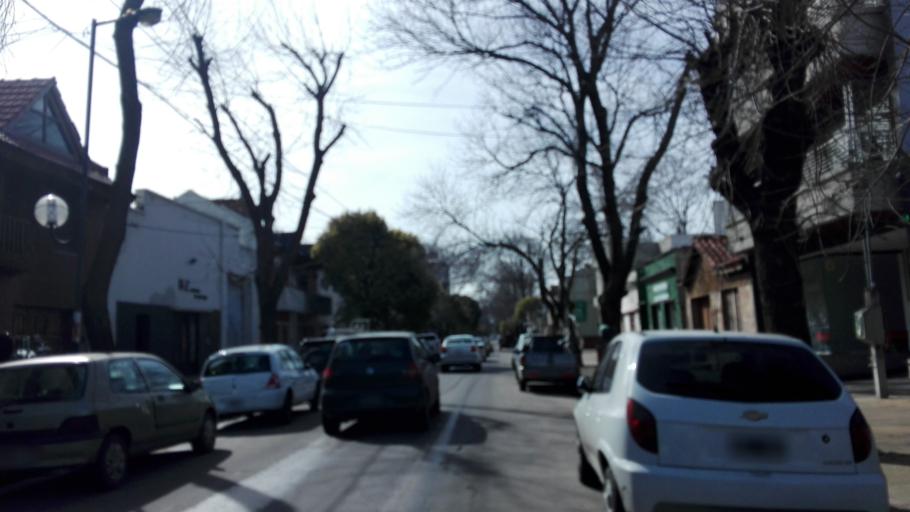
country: AR
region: Buenos Aires
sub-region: Partido de La Plata
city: La Plata
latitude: -34.9090
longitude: -57.9701
